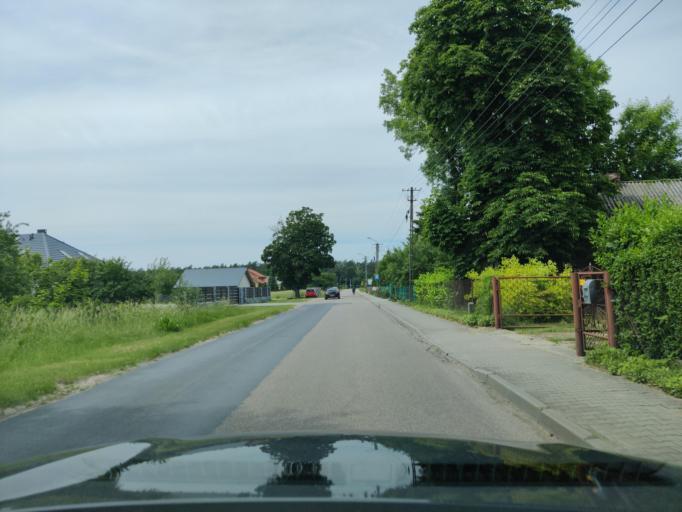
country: PL
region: Masovian Voivodeship
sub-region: Powiat wyszkowski
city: Rzasnik
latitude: 52.6989
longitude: 21.4045
